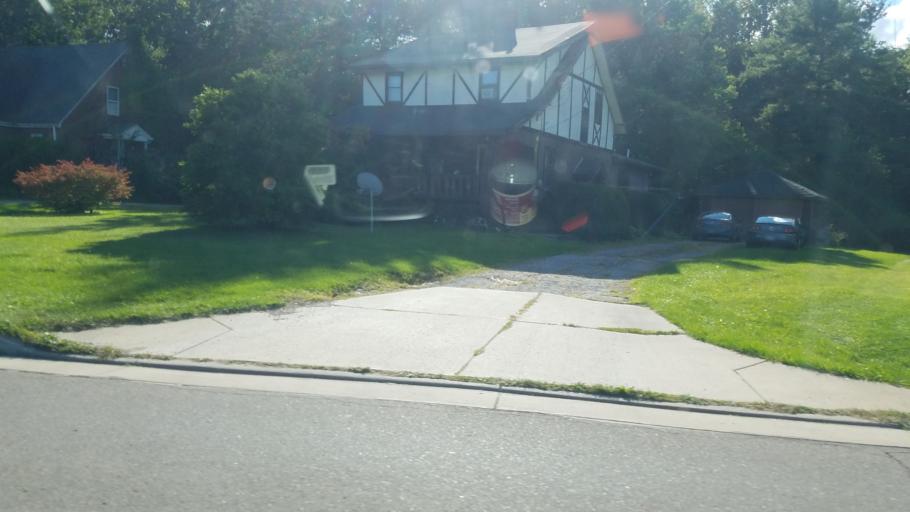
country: US
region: Ohio
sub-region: Mahoning County
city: Austintown
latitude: 41.1070
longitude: -80.7650
